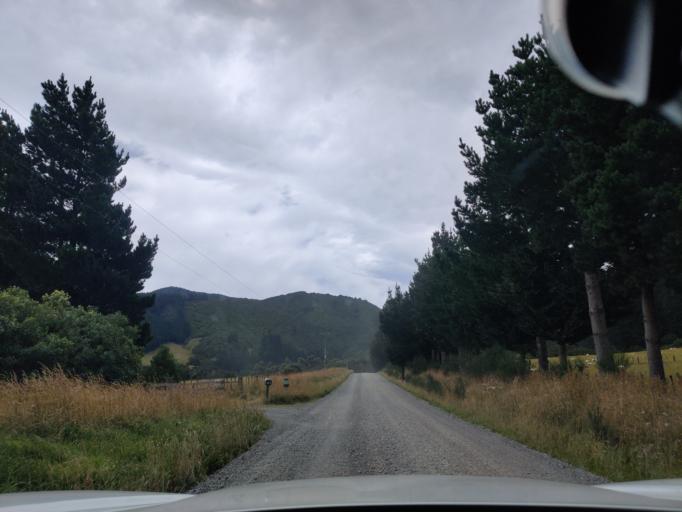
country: NZ
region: Wellington
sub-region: Masterton District
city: Masterton
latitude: -41.0379
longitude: 175.4018
